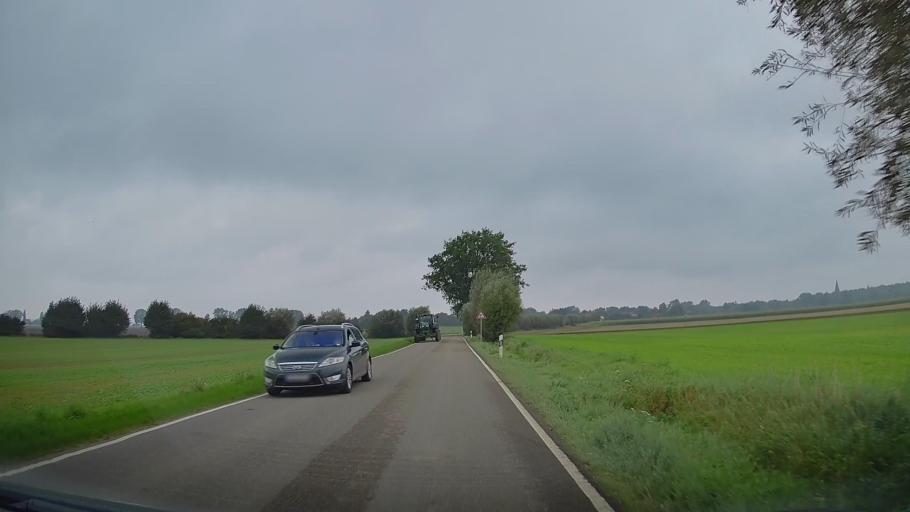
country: DE
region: Mecklenburg-Vorpommern
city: Blowatz
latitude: 53.9832
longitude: 11.5421
